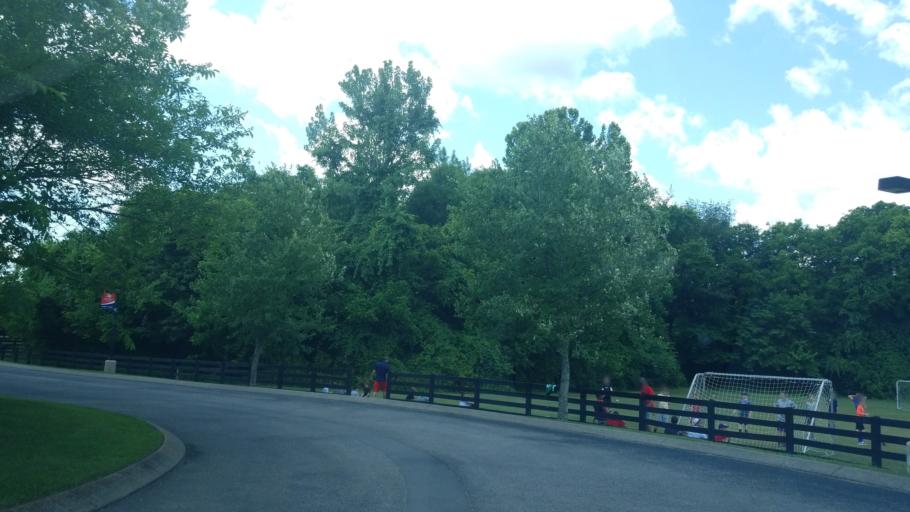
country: US
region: Tennessee
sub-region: Williamson County
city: Brentwood
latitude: 36.0349
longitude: -86.8191
